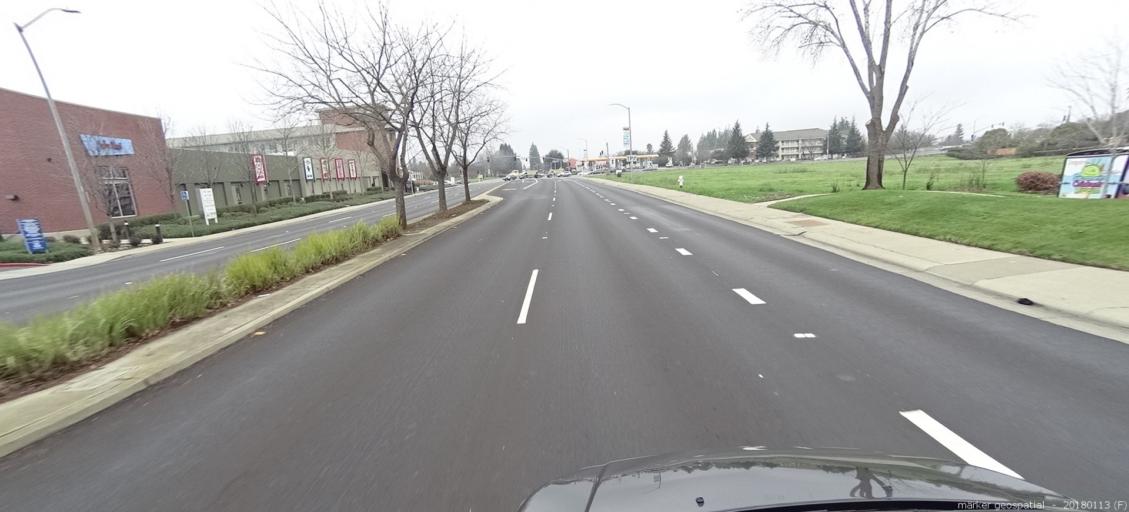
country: US
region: California
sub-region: Sacramento County
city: Rancho Cordova
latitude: 38.5883
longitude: -121.2847
